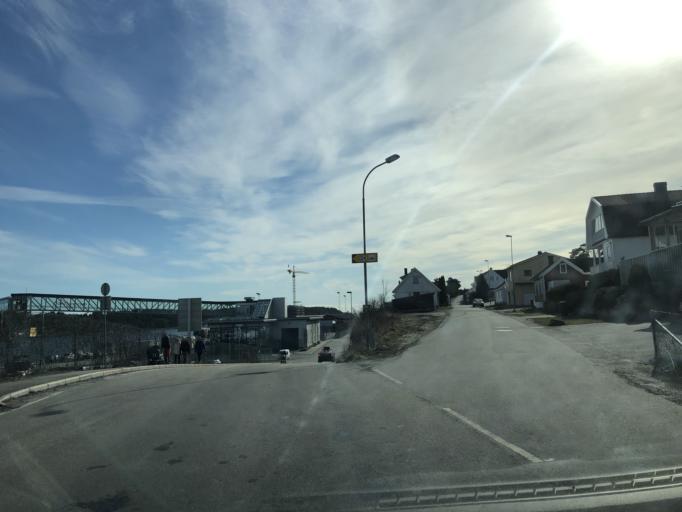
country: NO
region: Telemark
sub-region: Bamble
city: Langesund
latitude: 59.0076
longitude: 9.7456
